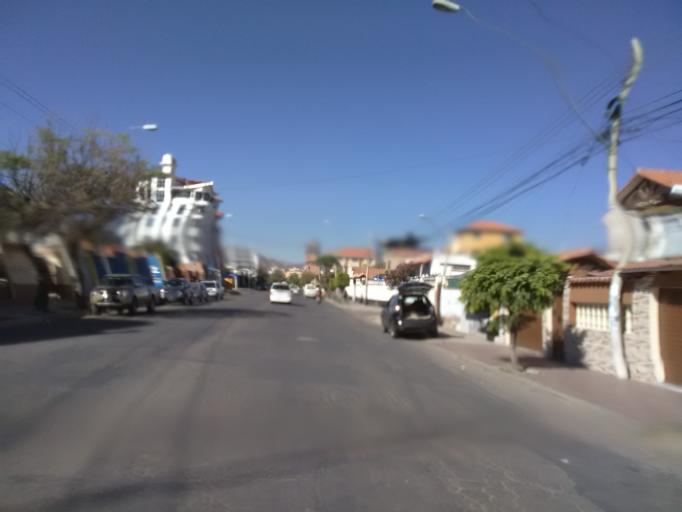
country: BO
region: Cochabamba
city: Cochabamba
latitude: -17.3880
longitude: -66.1773
